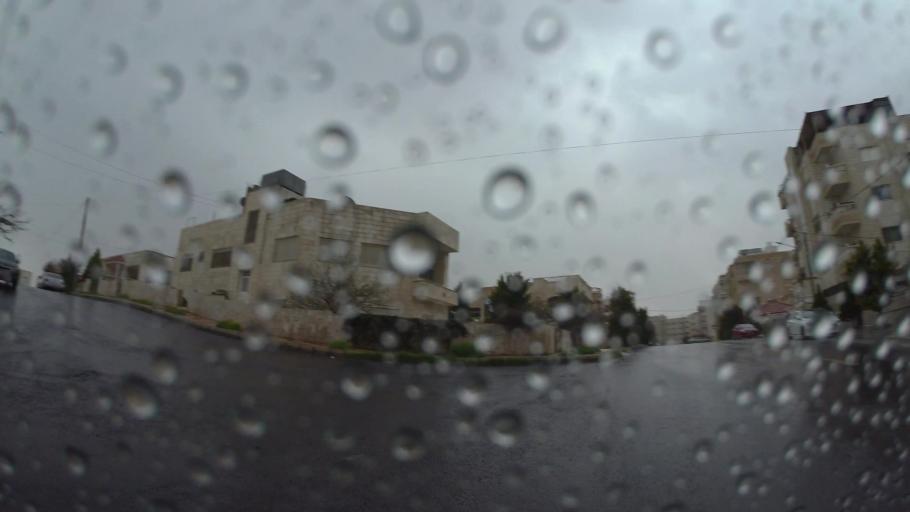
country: JO
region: Amman
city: Amman
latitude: 32.0036
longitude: 35.9577
